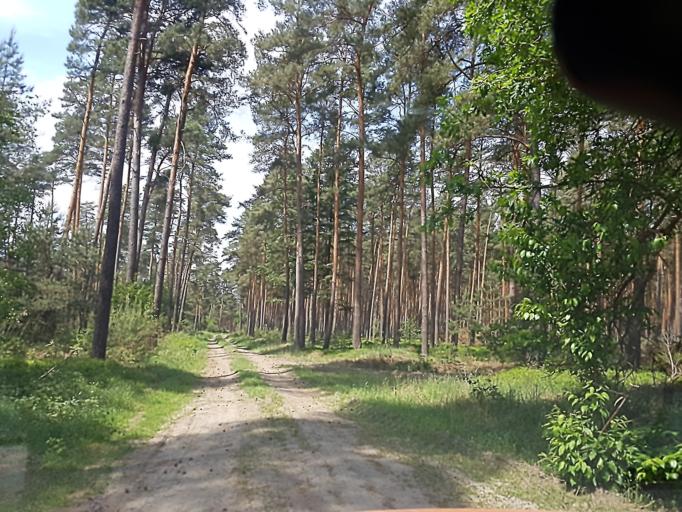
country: DE
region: Brandenburg
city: Gorzke
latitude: 52.1083
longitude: 12.3151
